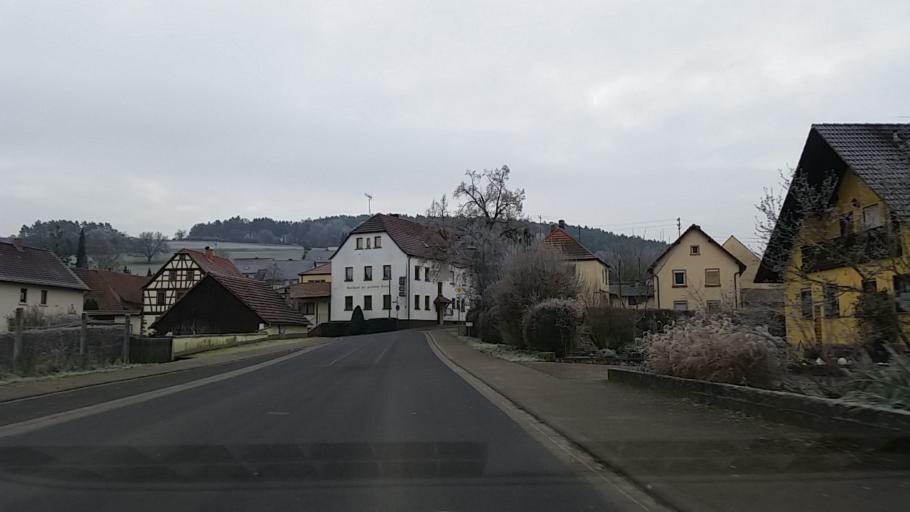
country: DE
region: Bavaria
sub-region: Regierungsbezirk Unterfranken
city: Eussenheim
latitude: 50.0134
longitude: 9.8634
